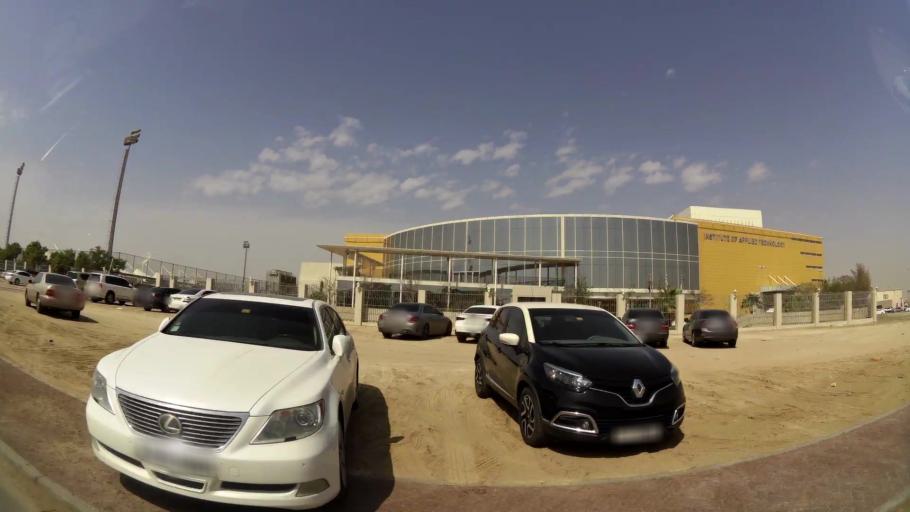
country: AE
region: Abu Dhabi
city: Abu Dhabi
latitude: 24.3129
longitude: 54.5605
